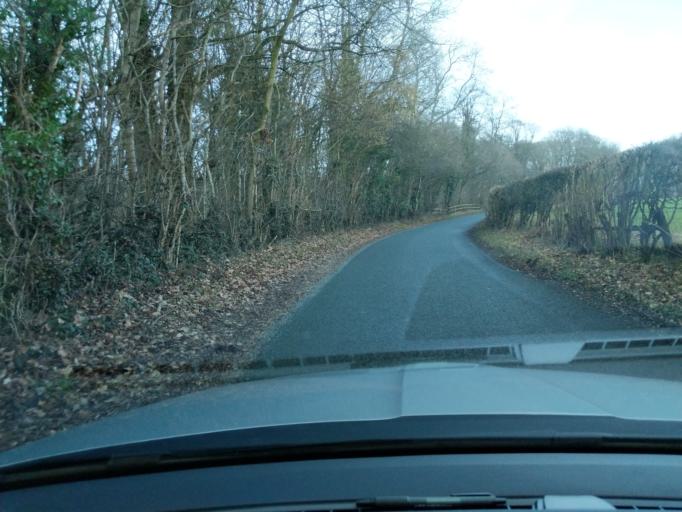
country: GB
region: England
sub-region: North Yorkshire
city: Catterick
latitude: 54.3723
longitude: -1.6733
